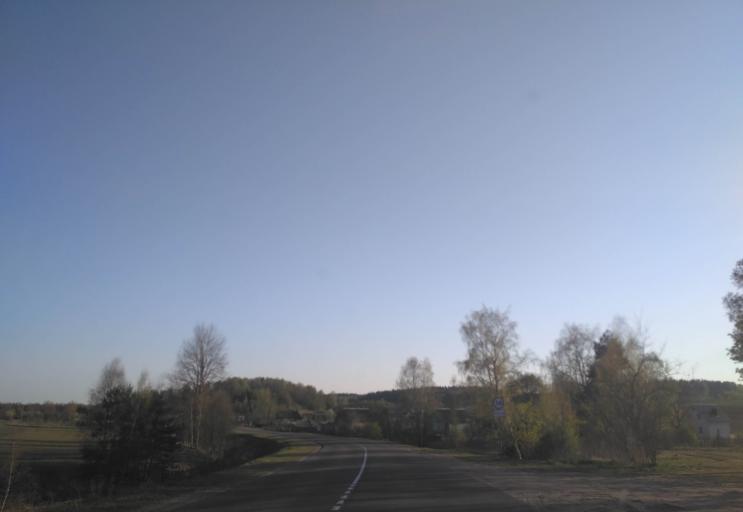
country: BY
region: Minsk
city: Radashkovichy
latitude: 54.1432
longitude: 27.2101
